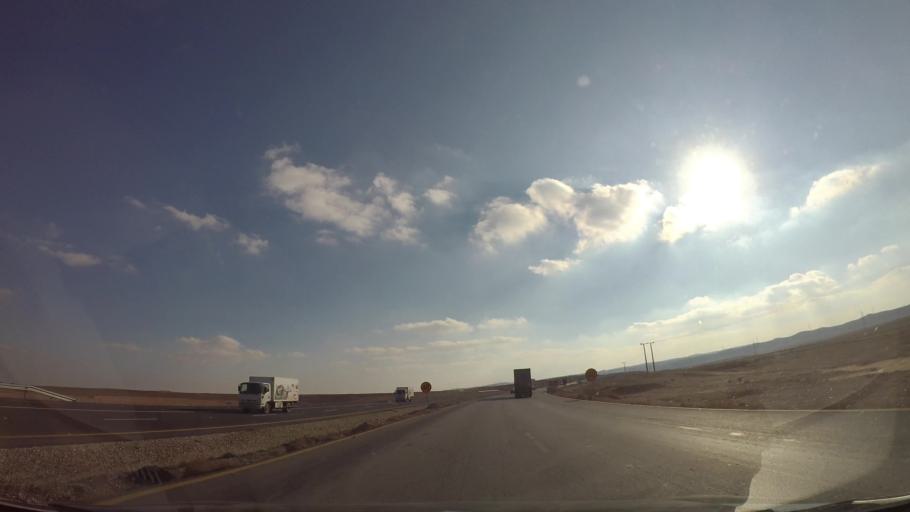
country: JO
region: Karak
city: Karak City
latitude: 31.1318
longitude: 36.0261
